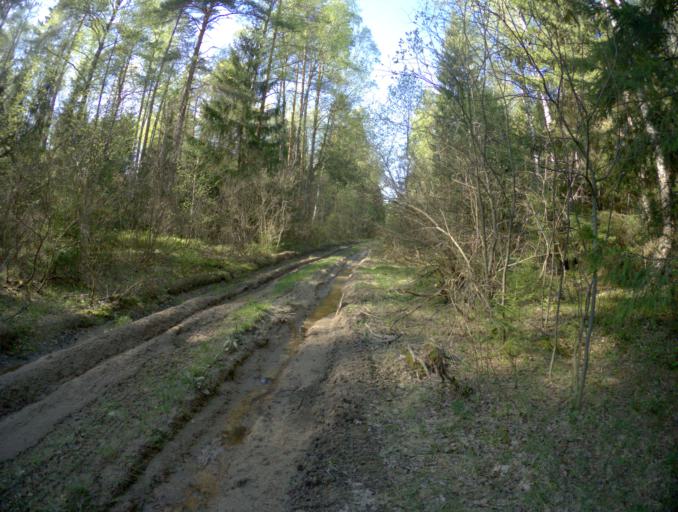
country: RU
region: Vladimir
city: Golovino
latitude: 55.9185
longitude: 40.4404
